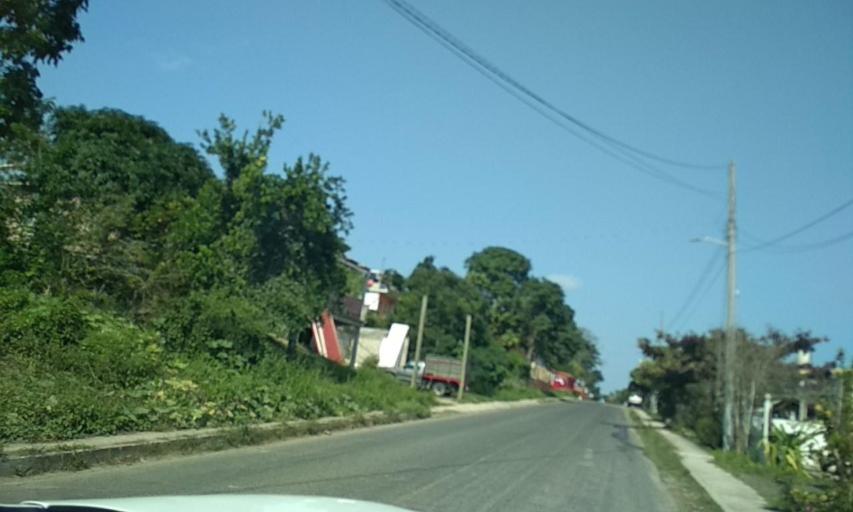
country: MX
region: Veracruz
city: Gutierrez Zamora
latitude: 20.3498
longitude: -97.1504
